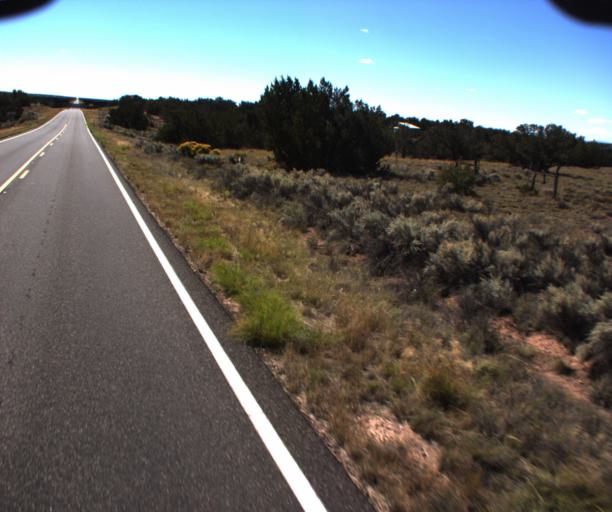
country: US
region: Arizona
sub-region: Apache County
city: Houck
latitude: 34.8946
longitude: -109.2381
